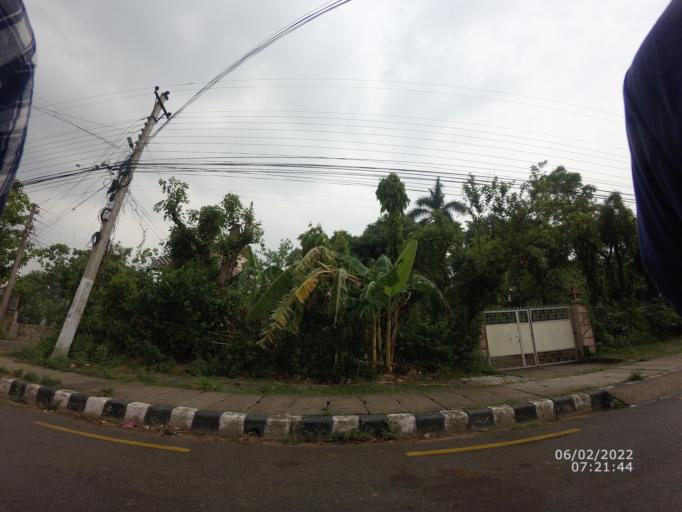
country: NP
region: Western Region
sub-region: Lumbini Zone
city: Bhairahawa
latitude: 27.4892
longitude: 83.4439
